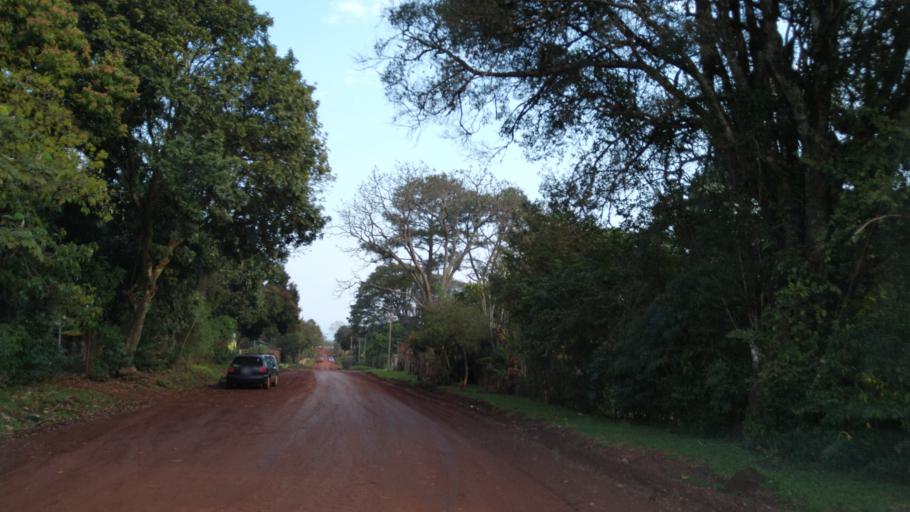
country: AR
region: Corrientes
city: San Carlos
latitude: -27.7445
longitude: -55.9014
